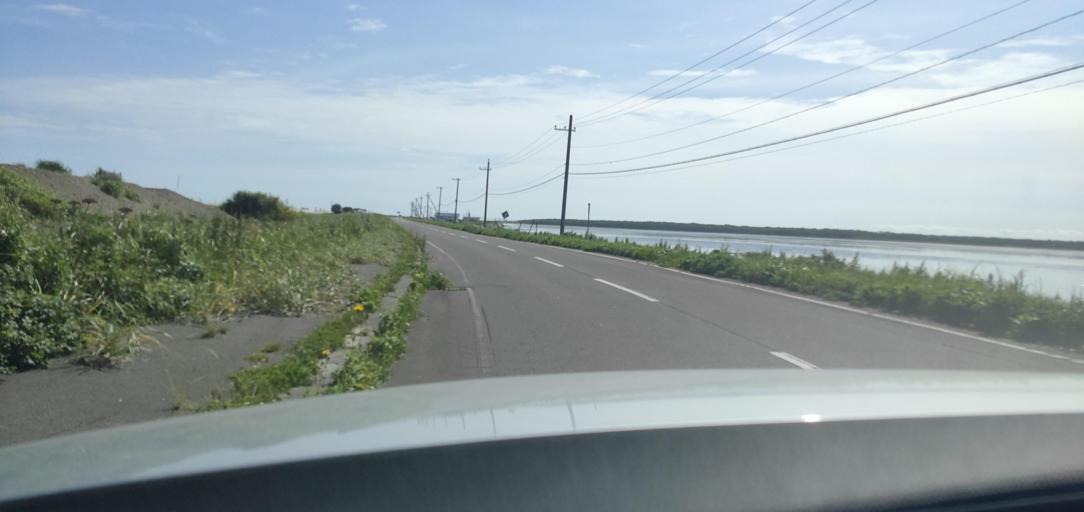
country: JP
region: Hokkaido
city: Shibetsu
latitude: 43.6135
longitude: 145.2488
